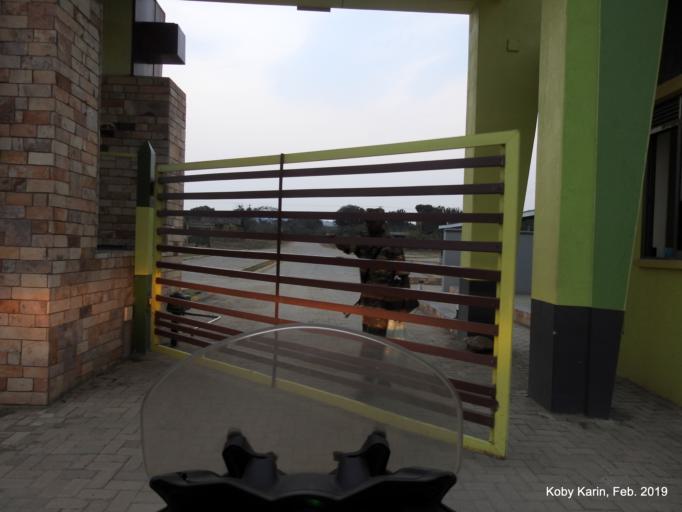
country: UG
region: Western Region
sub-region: Rubirizi District
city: Rubirizi
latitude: -0.1362
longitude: 29.9287
